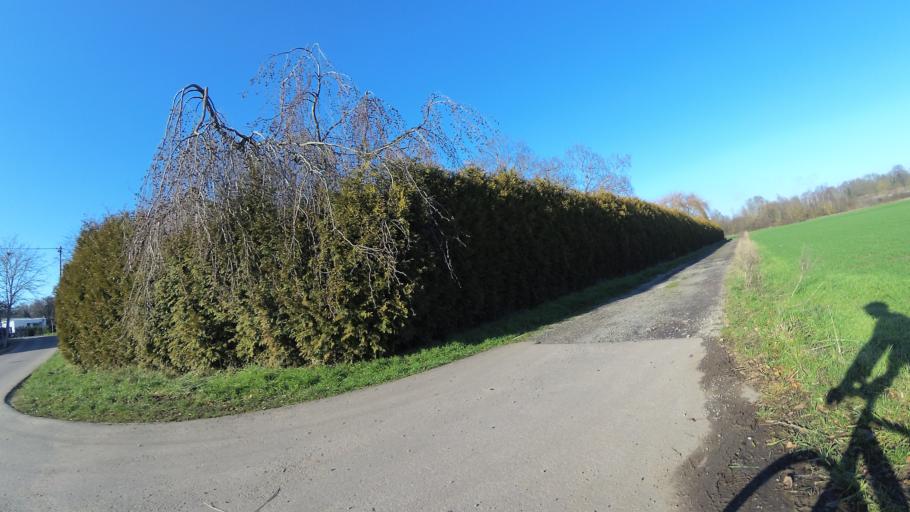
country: DE
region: Saarland
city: Saarlouis
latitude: 49.3014
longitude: 6.7417
